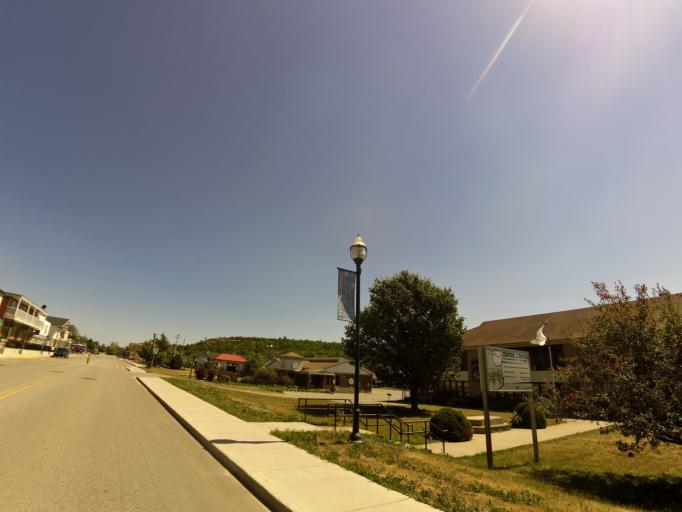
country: CA
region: Quebec
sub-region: Abitibi-Temiscamingue
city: Temiscaming
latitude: 46.7208
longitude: -79.0965
